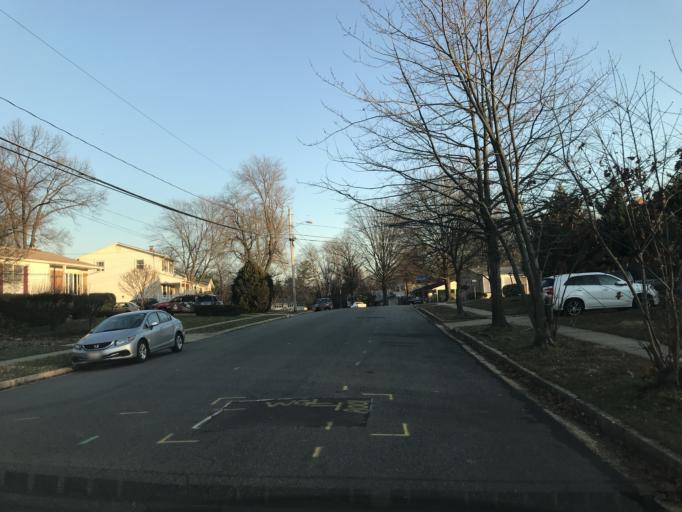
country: US
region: Virginia
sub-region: Fairfax County
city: Springfield
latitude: 38.7879
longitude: -77.1675
